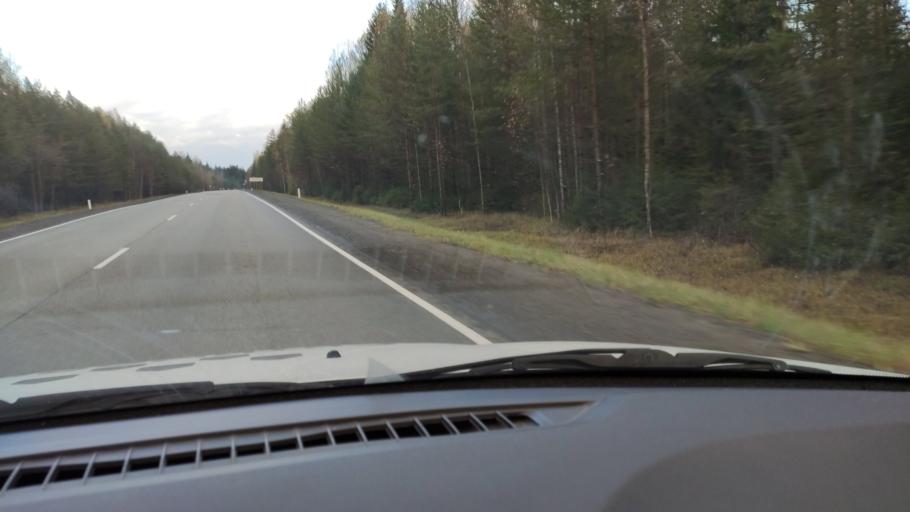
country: RU
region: Kirov
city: Belaya Kholunitsa
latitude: 58.9020
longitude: 50.9351
